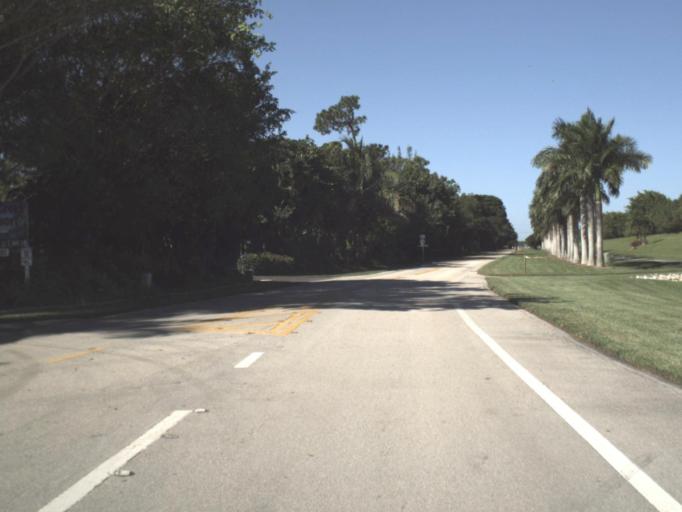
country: US
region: Florida
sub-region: Collier County
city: Naples
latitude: 26.1459
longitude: -81.7683
